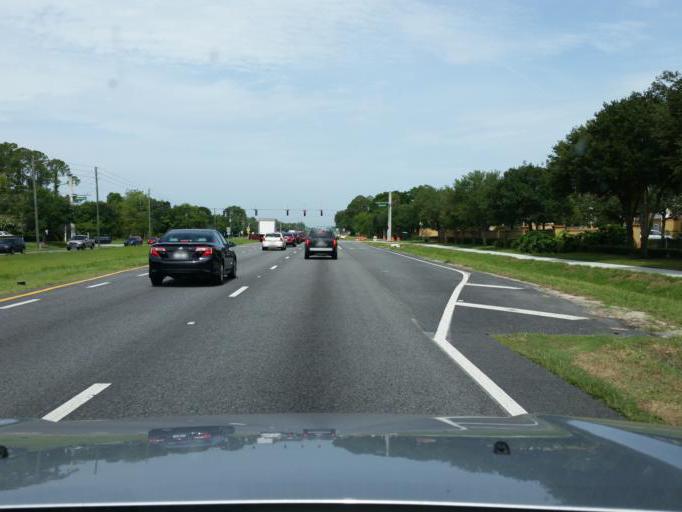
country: US
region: Florida
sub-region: Seminole County
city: Sanford
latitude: 28.8117
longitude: -81.3156
